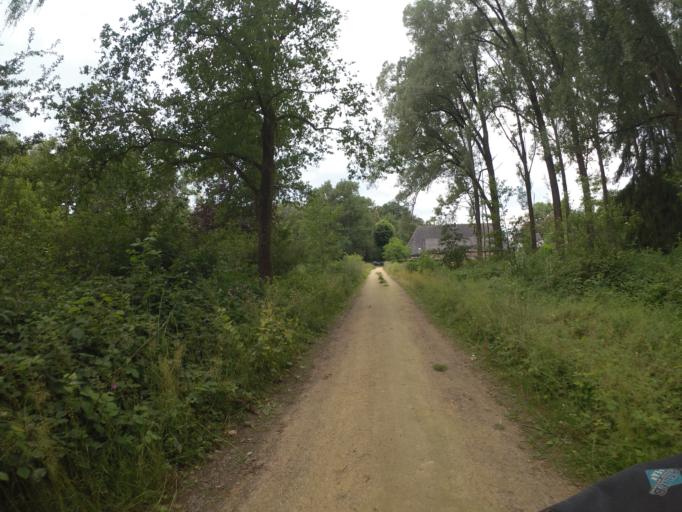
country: NL
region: North Brabant
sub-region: Gemeente Oirschot
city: Oirschot
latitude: 51.5419
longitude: 5.3459
